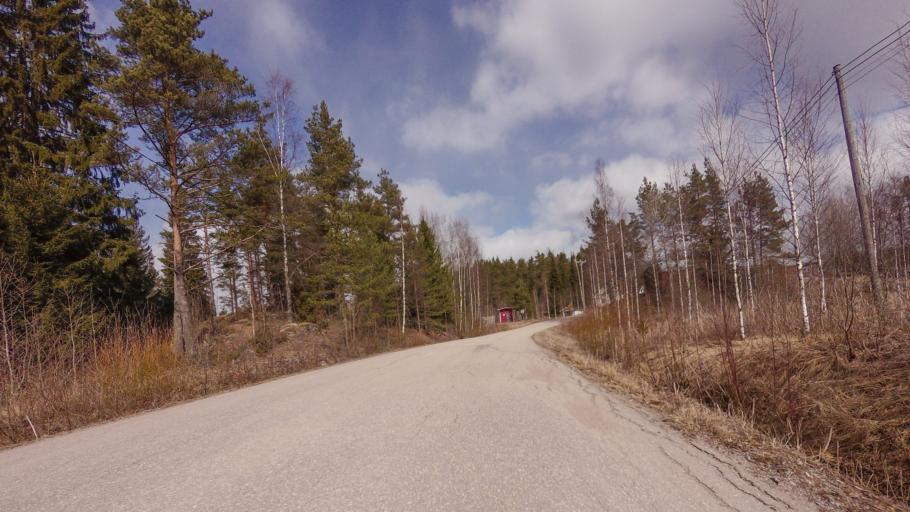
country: FI
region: Varsinais-Suomi
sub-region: Salo
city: Suomusjaervi
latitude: 60.3174
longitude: 23.6443
